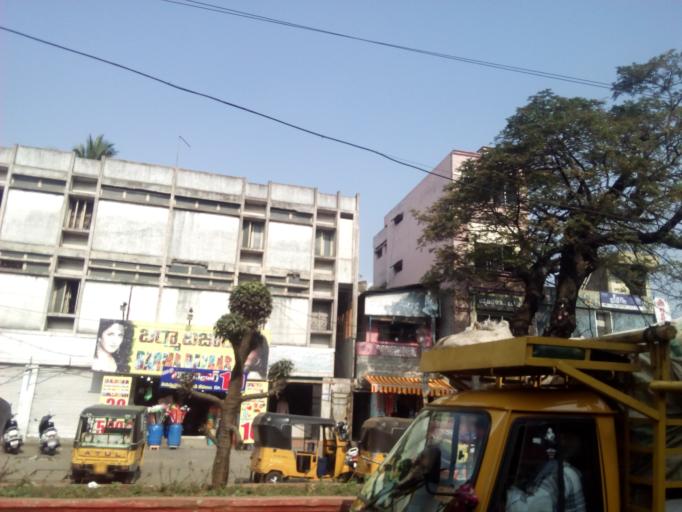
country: IN
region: Andhra Pradesh
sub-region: East Godavari
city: Rajahmundry
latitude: 16.9951
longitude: 81.7747
